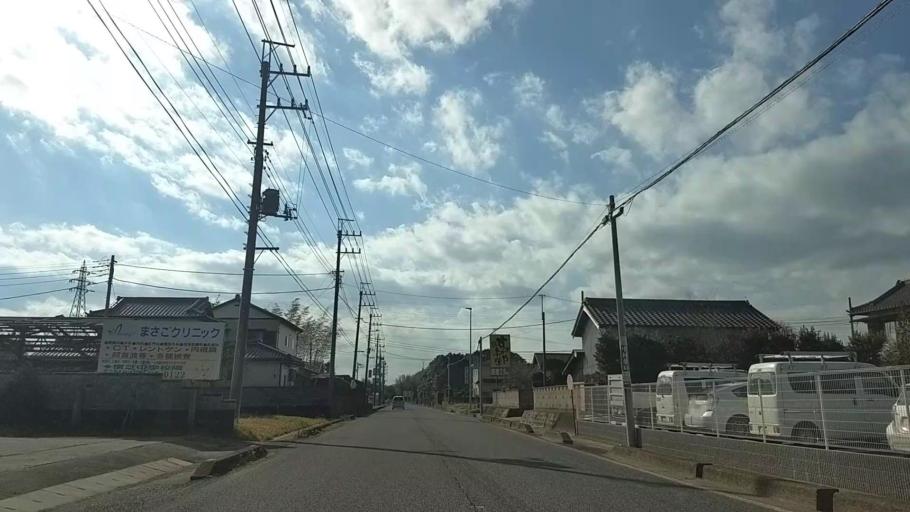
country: JP
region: Chiba
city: Naruto
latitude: 35.6515
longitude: 140.4682
